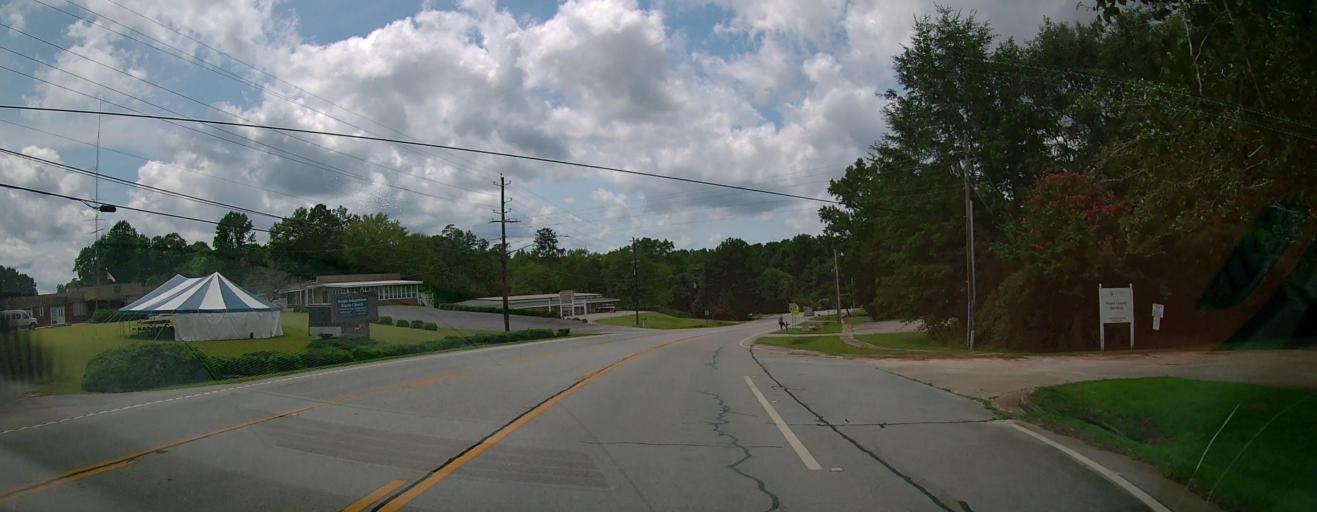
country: US
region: Georgia
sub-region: Heard County
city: Franklin
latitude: 33.2718
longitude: -85.0917
